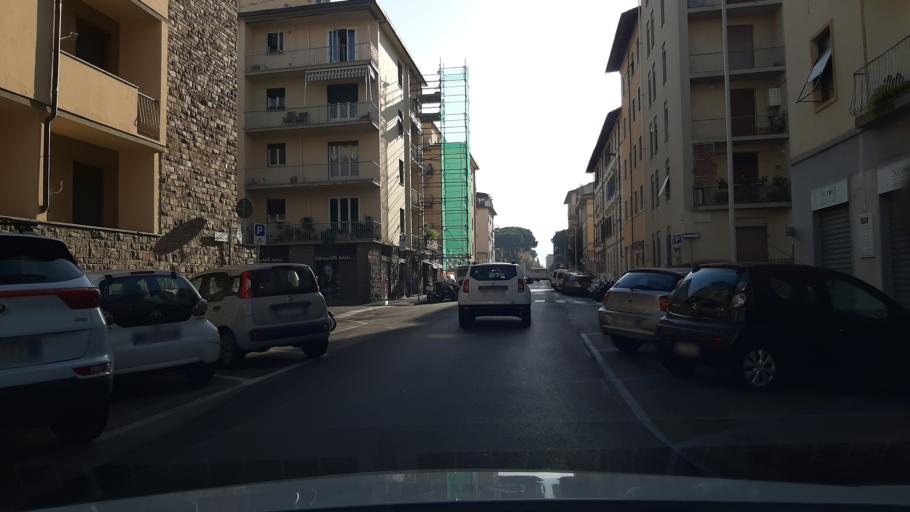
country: IT
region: Tuscany
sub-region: Province of Florence
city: Fiesole
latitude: 43.7826
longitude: 11.2879
